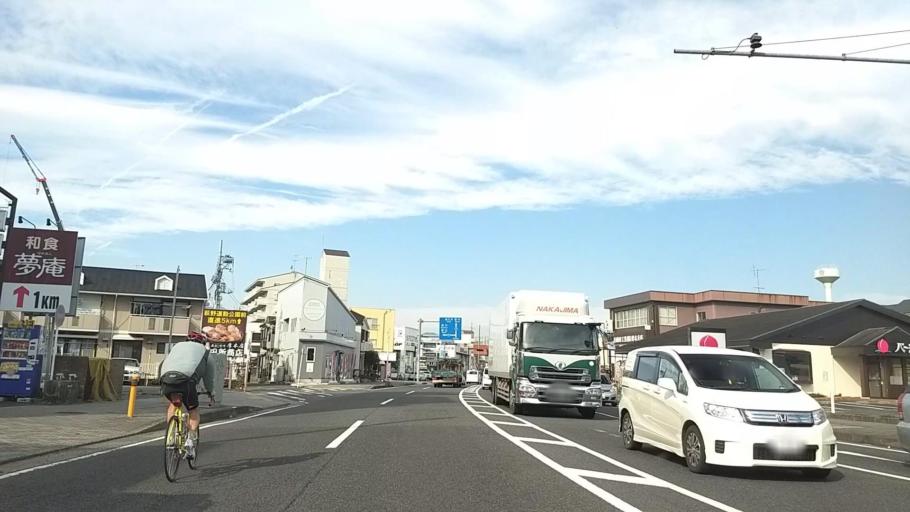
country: JP
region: Kanagawa
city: Atsugi
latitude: 35.4501
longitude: 139.3568
